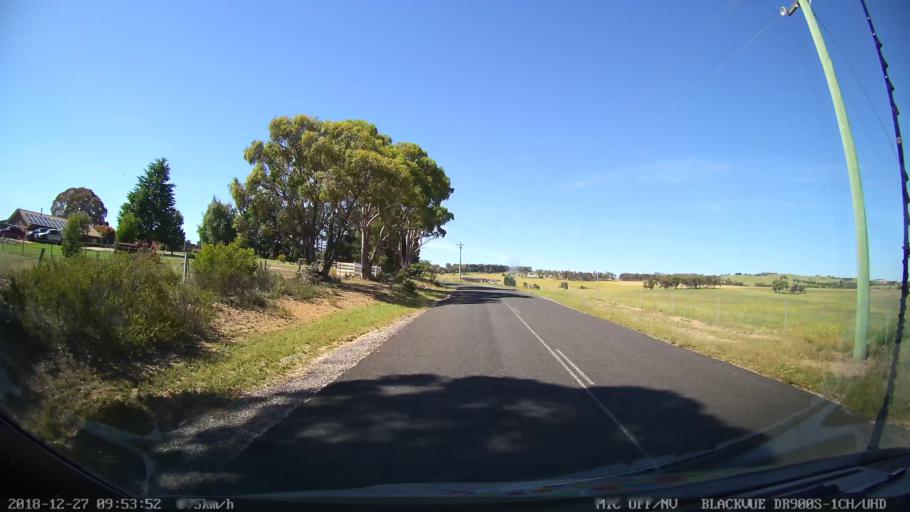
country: AU
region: New South Wales
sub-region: Lithgow
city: Portland
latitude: -33.3869
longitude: 149.9860
